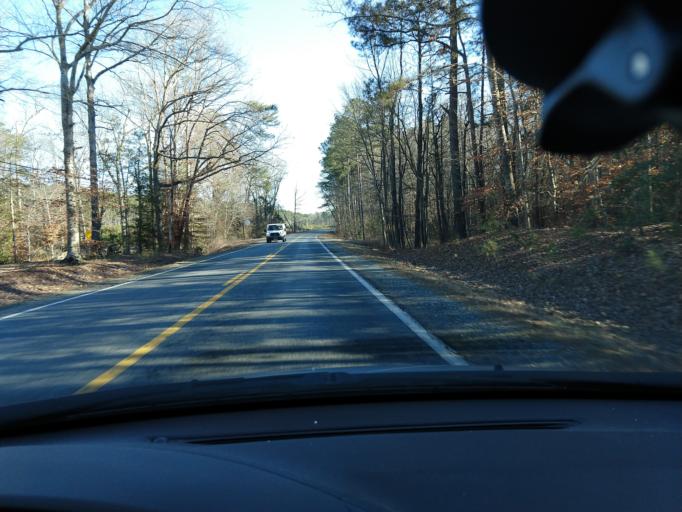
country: US
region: Virginia
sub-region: Charles City County
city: Charles City
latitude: 37.3231
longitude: -76.9772
